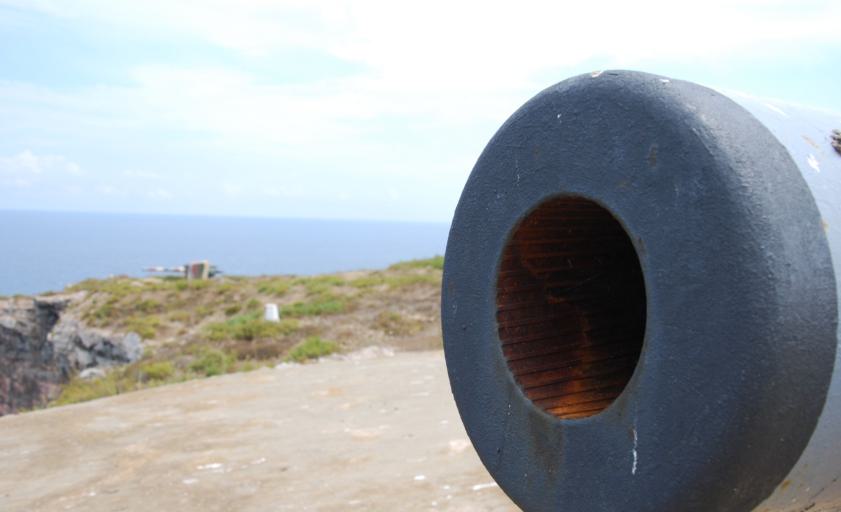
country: ES
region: Balearic Islands
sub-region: Illes Balears
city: Es Castell
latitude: 39.8756
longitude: 4.3247
